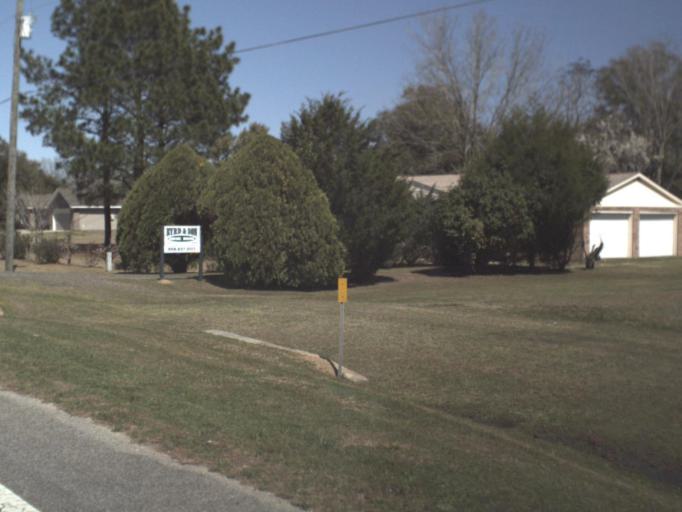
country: US
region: Florida
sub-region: Gadsden County
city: Gretna
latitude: 30.6971
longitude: -84.6242
